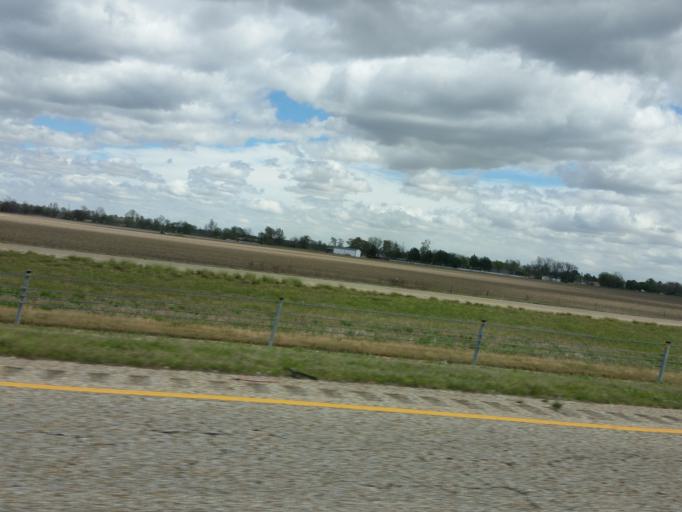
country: US
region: Arkansas
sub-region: Poinsett County
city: Trumann
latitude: 35.6400
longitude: -90.5092
